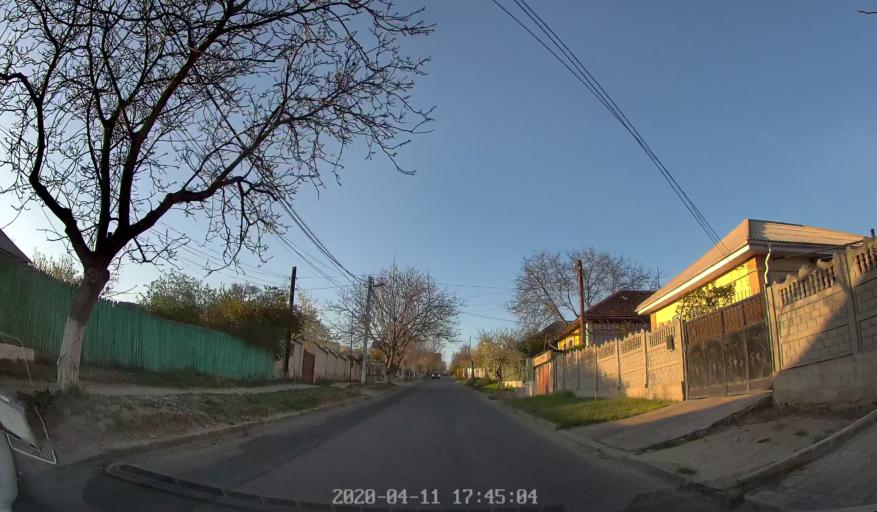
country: MD
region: Chisinau
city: Chisinau
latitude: 46.9821
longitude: 28.8231
